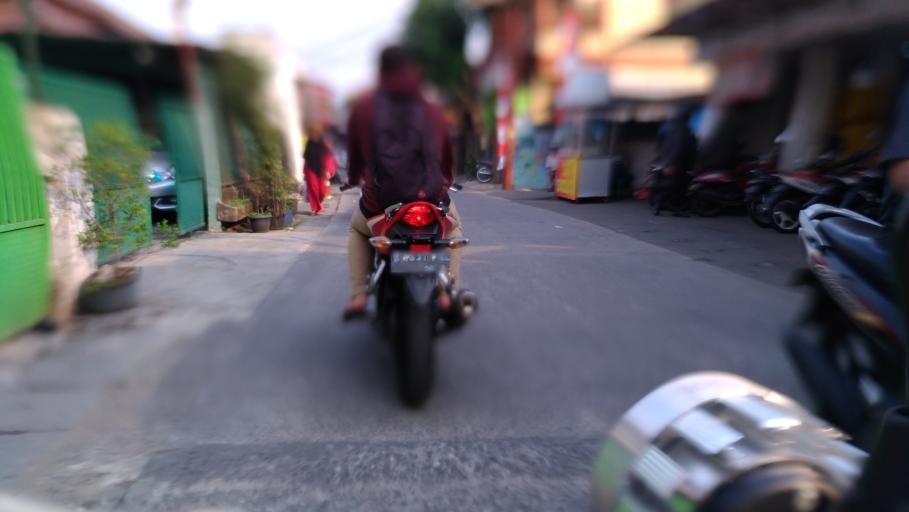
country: ID
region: West Java
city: Depok
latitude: -6.3525
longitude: 106.8726
